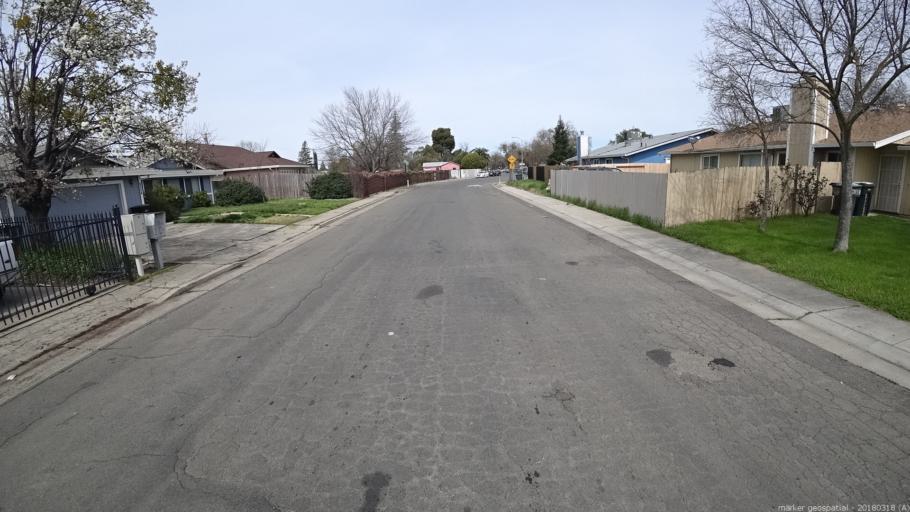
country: US
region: California
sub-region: Sacramento County
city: Parkway
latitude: 38.5167
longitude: -121.4478
